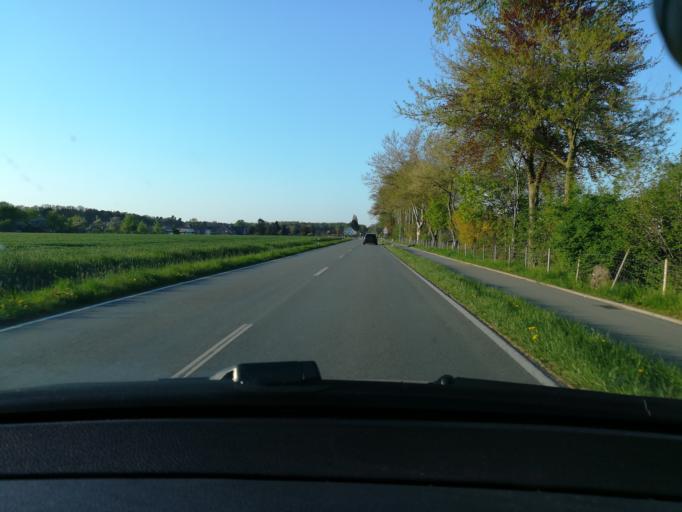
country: DE
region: North Rhine-Westphalia
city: Versmold
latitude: 52.0578
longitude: 8.1575
